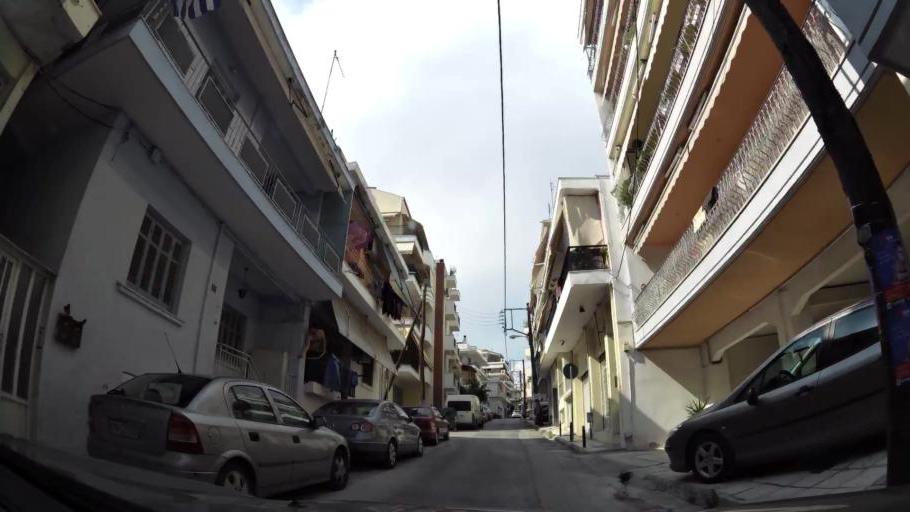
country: GR
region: Central Macedonia
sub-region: Nomos Thessalonikis
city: Polichni
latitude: 40.6602
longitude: 22.9446
